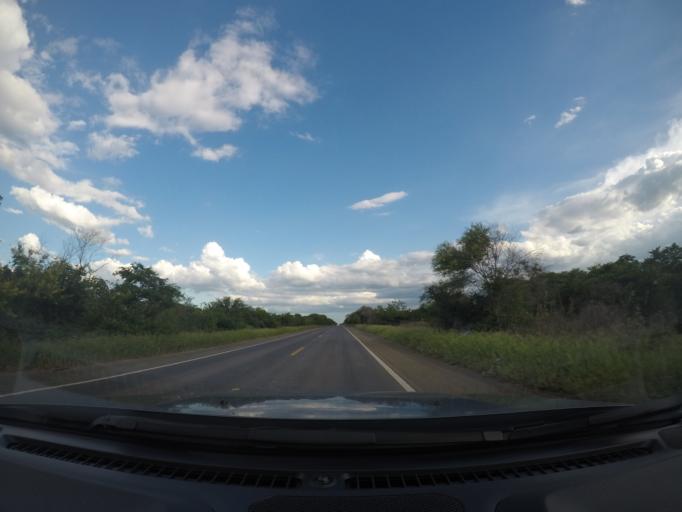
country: BR
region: Bahia
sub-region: Oliveira Dos Brejinhos
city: Beira Rio
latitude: -12.1999
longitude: -42.8139
